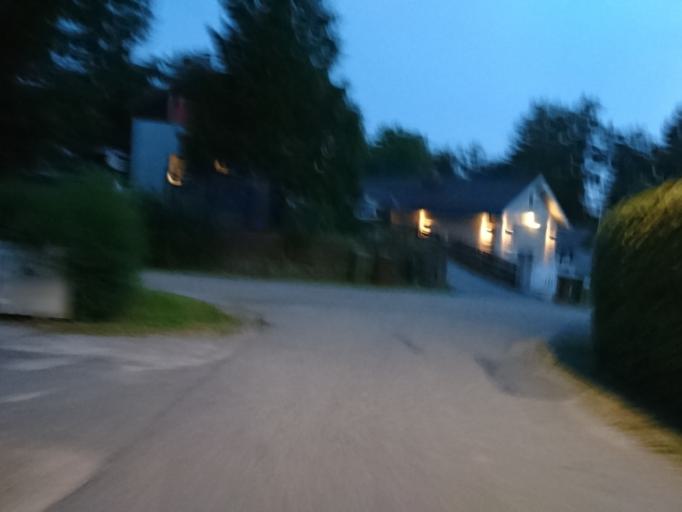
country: SE
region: Stockholm
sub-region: Huddinge Kommun
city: Segeltorp
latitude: 59.2762
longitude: 17.9365
